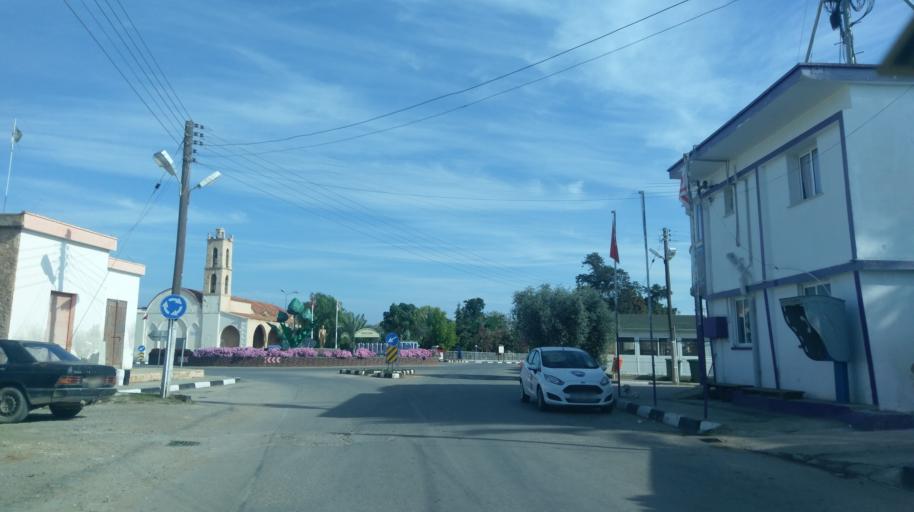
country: CY
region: Ammochostos
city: Trikomo
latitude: 35.1994
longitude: 33.8601
